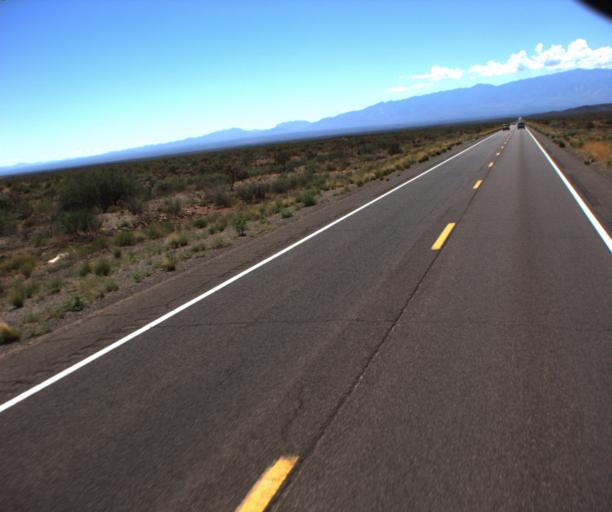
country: US
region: Arizona
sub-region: Graham County
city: Safford
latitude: 32.8286
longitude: -109.4560
